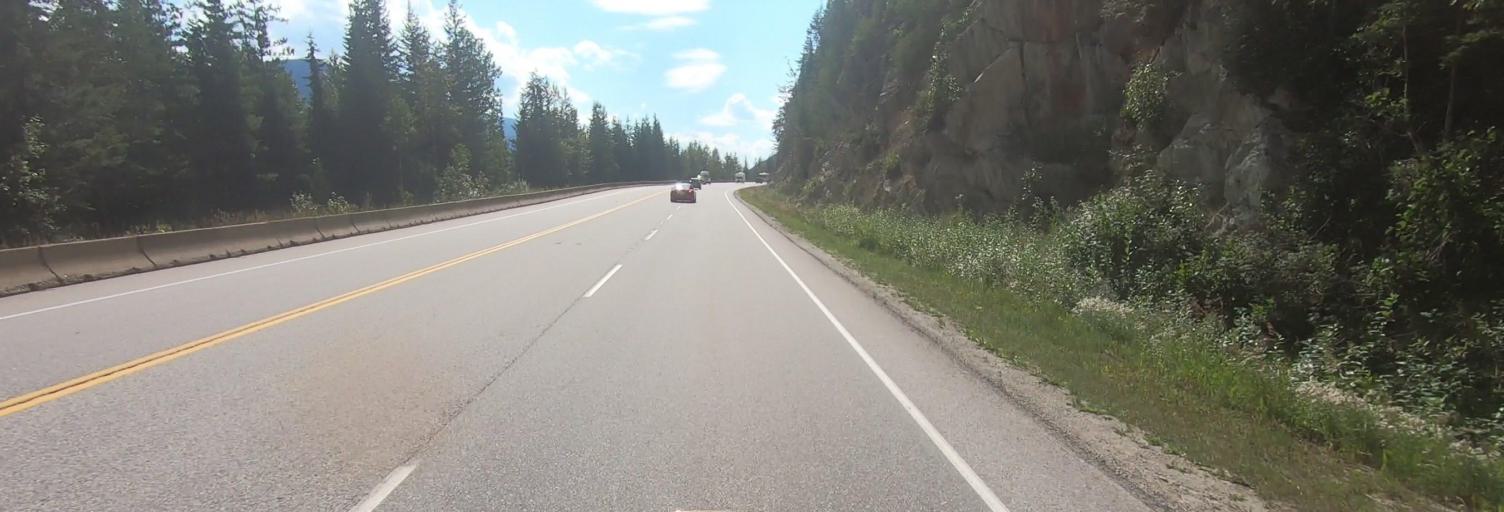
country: CA
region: British Columbia
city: Golden
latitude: 51.3633
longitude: -117.4402
